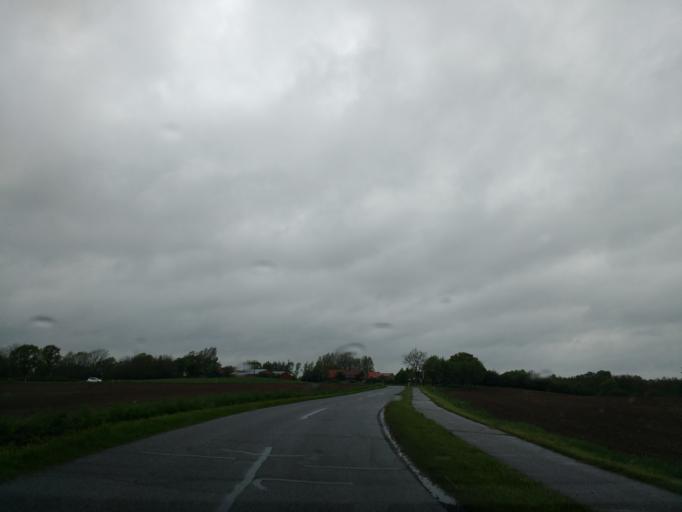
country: DE
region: Schleswig-Holstein
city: Waabs
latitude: 54.5237
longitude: 9.9693
